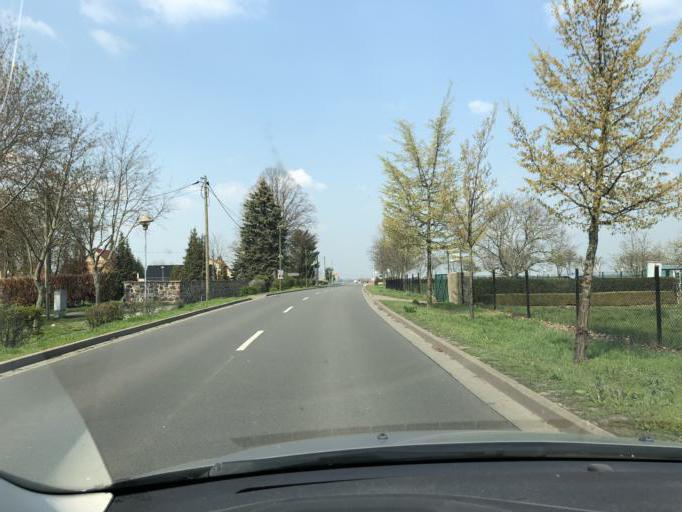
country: DE
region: Saxony-Anhalt
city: Zorbig
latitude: 51.5862
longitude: 12.1373
